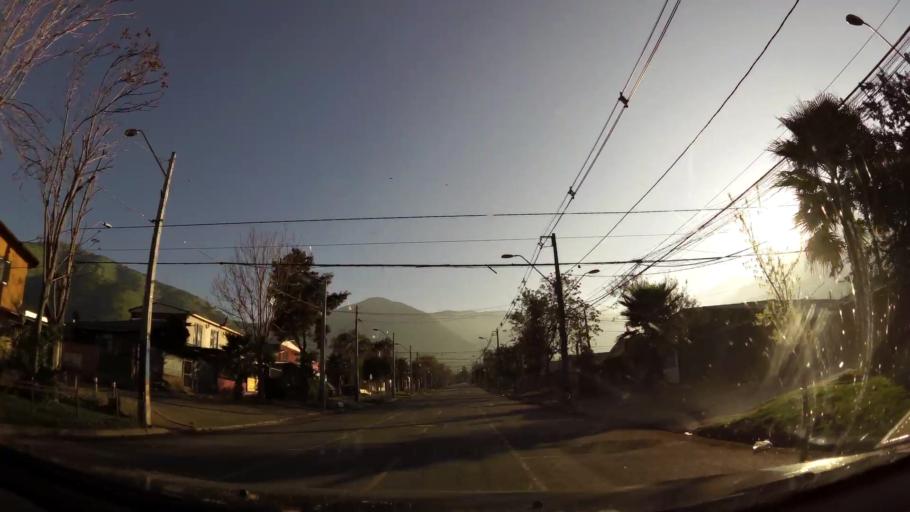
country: CL
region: Santiago Metropolitan
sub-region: Provincia de Chacabuco
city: Chicureo Abajo
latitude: -33.3654
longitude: -70.6309
